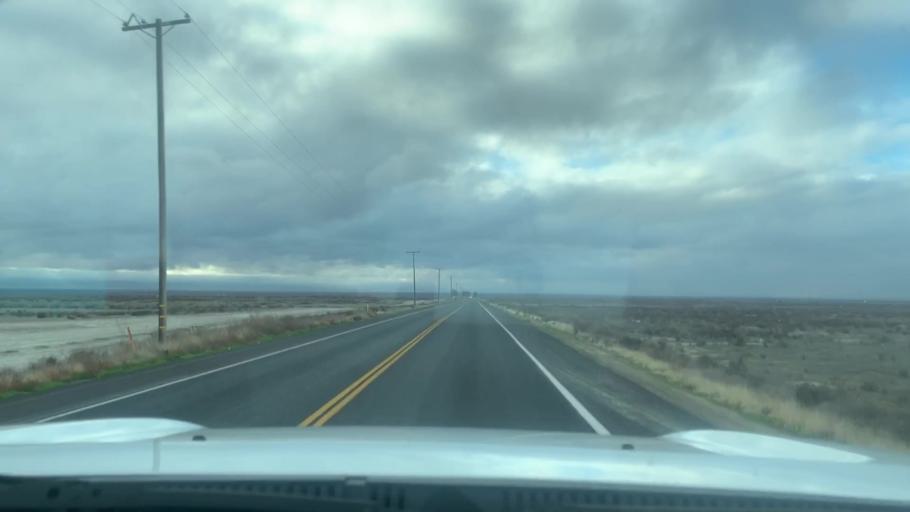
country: US
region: California
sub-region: Kern County
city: Buttonwillow
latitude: 35.4994
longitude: -119.5503
